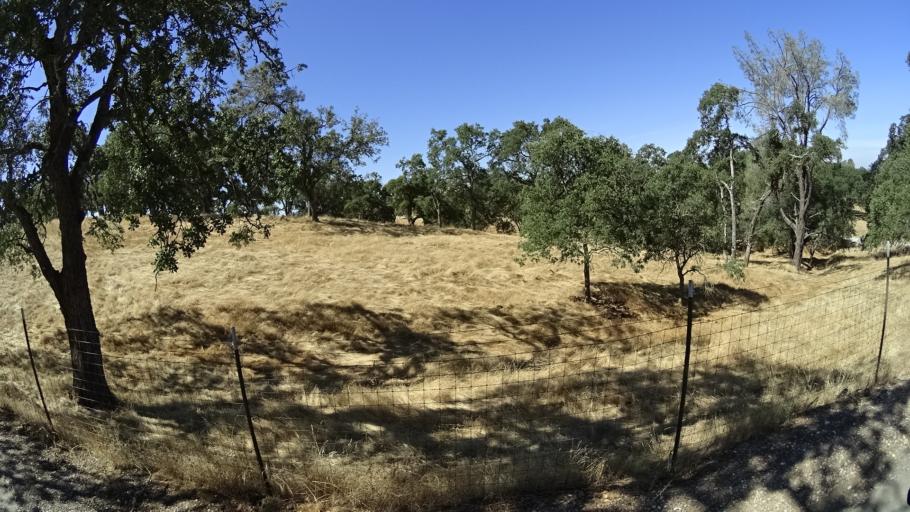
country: US
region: California
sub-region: Calaveras County
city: Valley Springs
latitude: 38.2288
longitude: -120.8598
